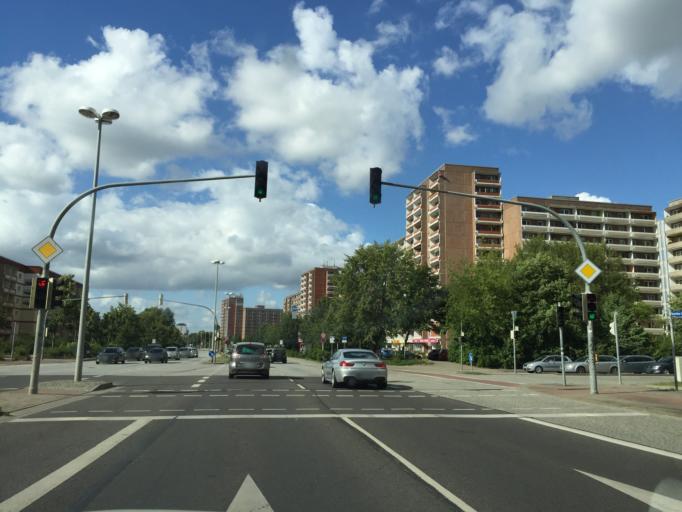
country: DE
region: Mecklenburg-Vorpommern
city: Neubrandenburg
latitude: 53.5412
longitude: 13.2653
